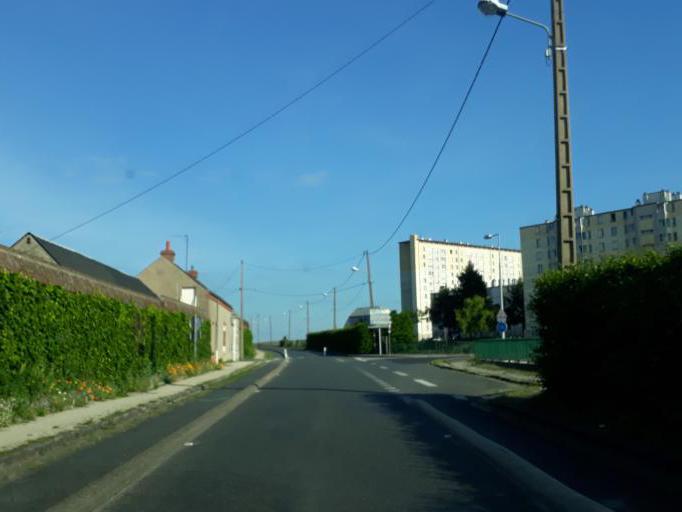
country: FR
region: Centre
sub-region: Departement du Loiret
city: Orleans
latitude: 47.9159
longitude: 1.9101
